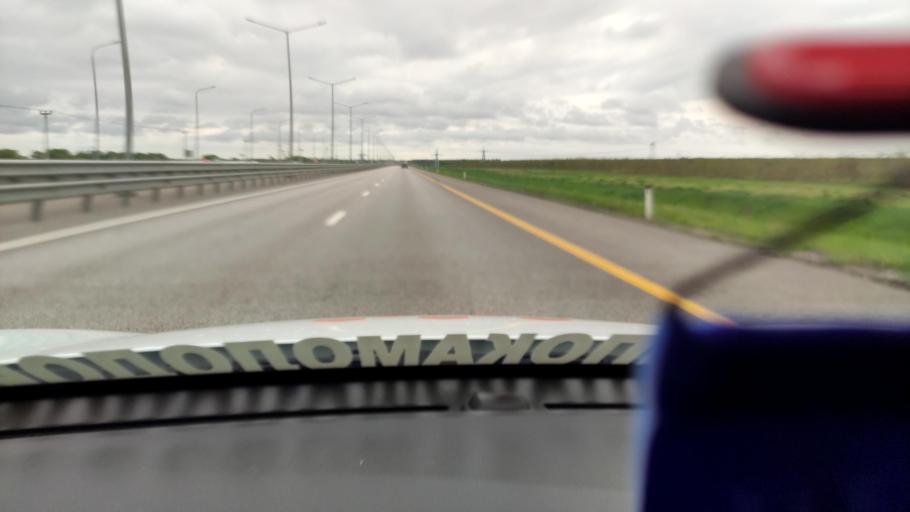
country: RU
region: Voronezj
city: Podkletnoye
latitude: 51.5587
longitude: 39.4840
